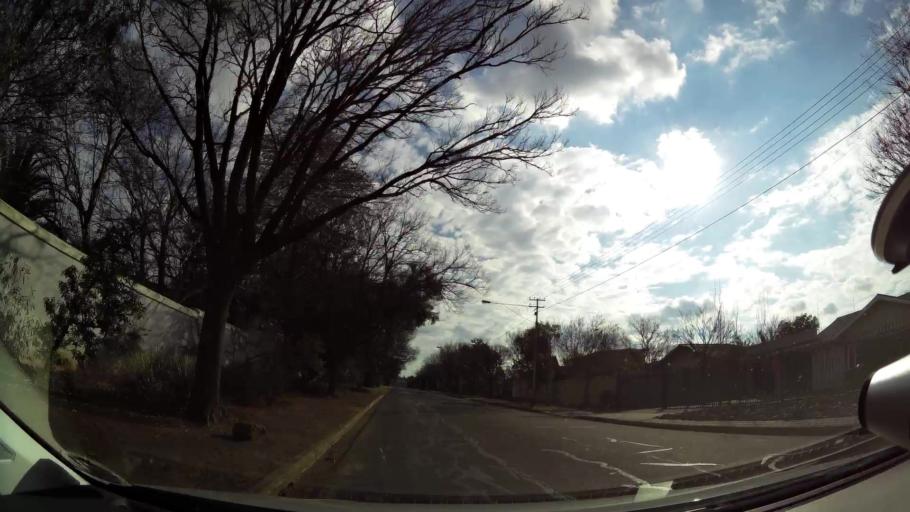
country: ZA
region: Orange Free State
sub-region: Mangaung Metropolitan Municipality
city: Bloemfontein
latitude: -29.0785
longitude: 26.2141
